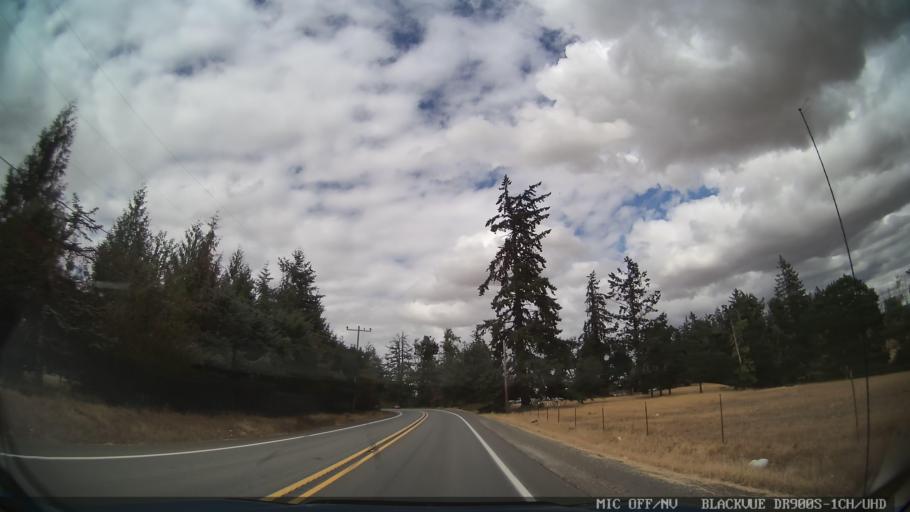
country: US
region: Oregon
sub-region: Marion County
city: Sublimity
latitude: 44.8500
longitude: -122.7940
